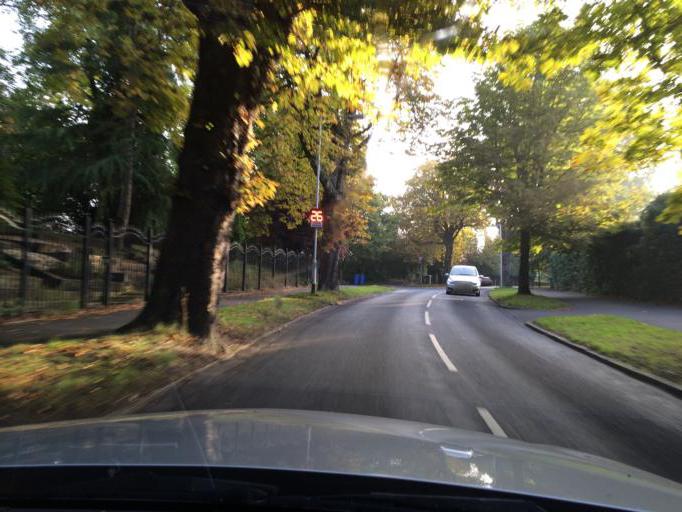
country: GB
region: England
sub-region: Borough of Stockport
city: Bramhall
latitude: 53.3770
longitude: -2.1679
